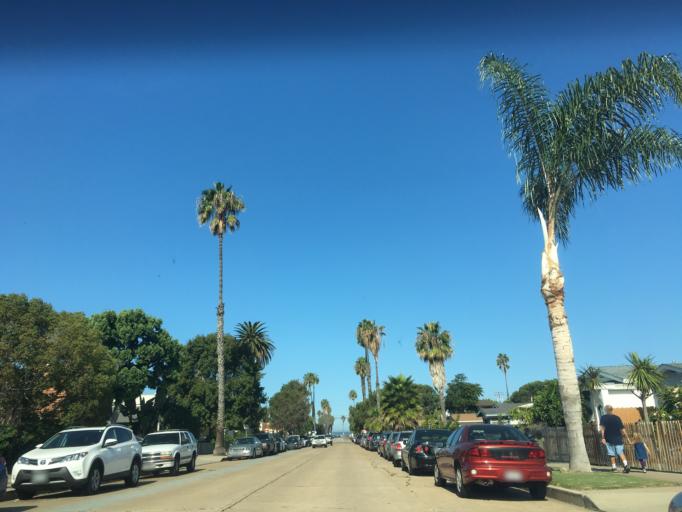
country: US
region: California
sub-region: San Diego County
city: Coronado
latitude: 32.7477
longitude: -117.2482
